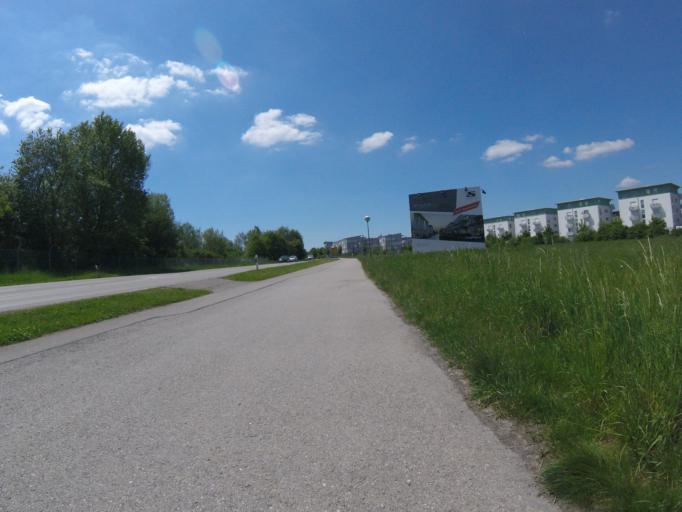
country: DE
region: Bavaria
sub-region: Upper Bavaria
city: Unterhaching
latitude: 48.0713
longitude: 11.6198
